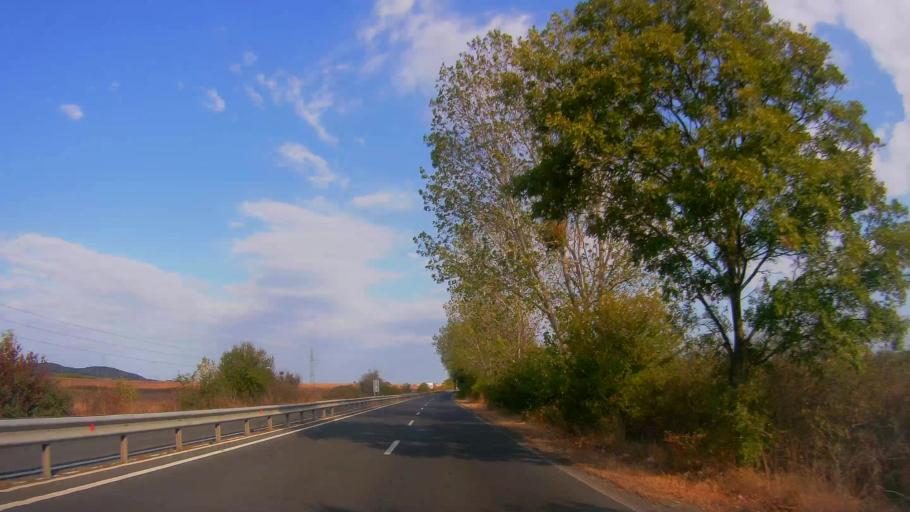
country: BG
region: Burgas
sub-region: Obshtina Sozopol
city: Chernomorets
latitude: 42.4126
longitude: 27.6478
